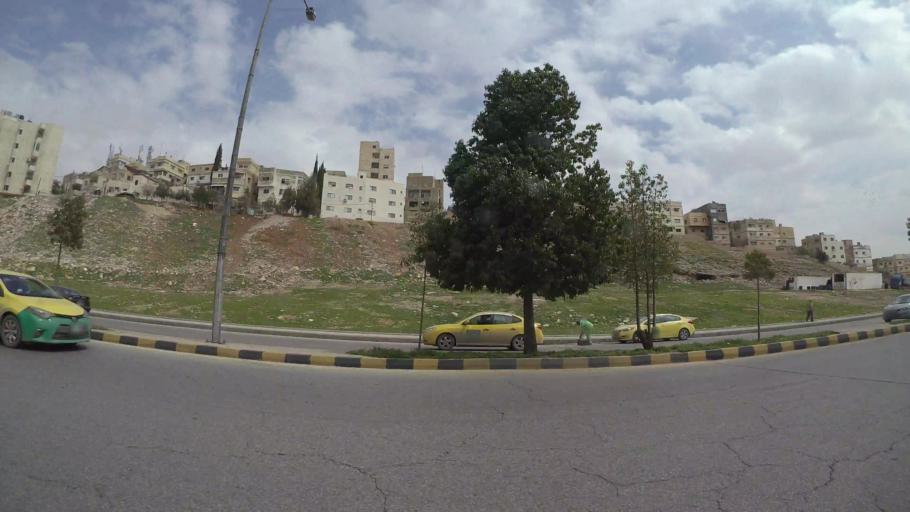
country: JO
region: Amman
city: Amman
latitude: 31.9772
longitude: 35.9189
